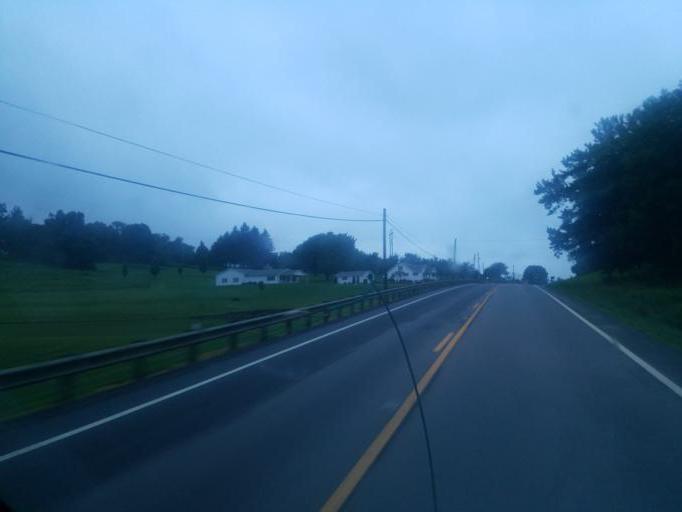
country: US
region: Ohio
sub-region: Carroll County
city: Carrollton
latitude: 40.5483
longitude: -81.0431
